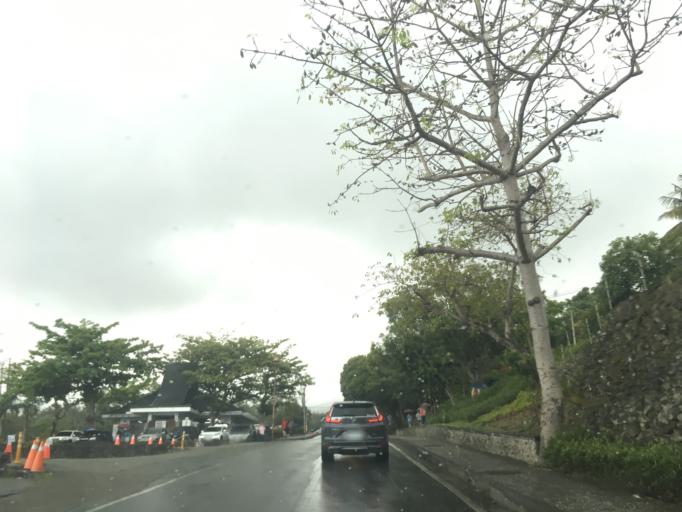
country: TW
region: Taiwan
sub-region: Taitung
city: Taitung
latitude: 22.8681
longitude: 121.2188
